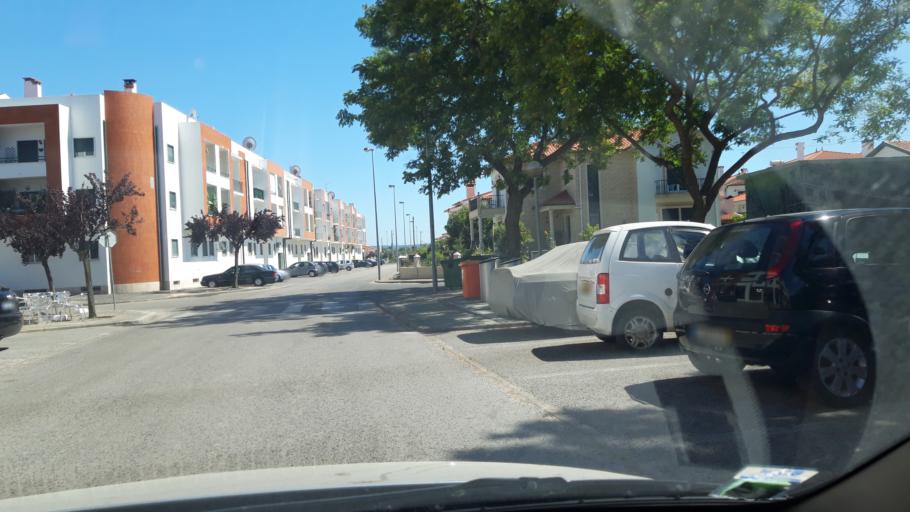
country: PT
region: Santarem
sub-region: Entroncamento
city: Entroncamento
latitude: 39.4646
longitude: -8.4528
